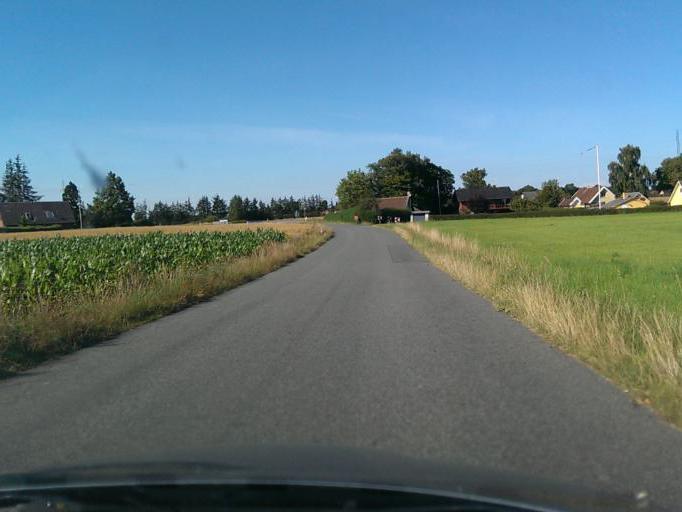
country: DK
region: Central Jutland
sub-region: Odder Kommune
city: Odder
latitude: 55.9192
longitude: 10.1414
